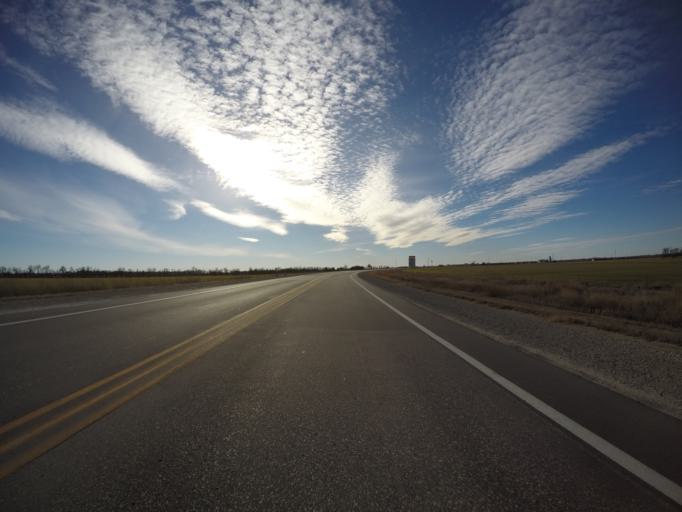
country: US
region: Kansas
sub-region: McPherson County
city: McPherson
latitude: 38.3721
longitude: -97.6047
